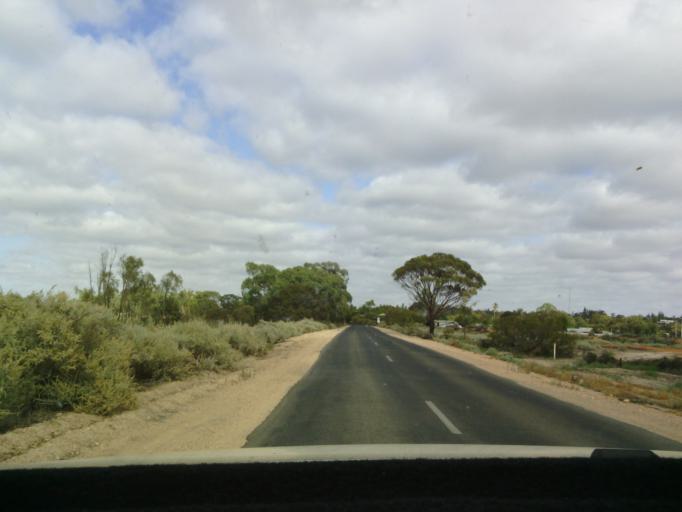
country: AU
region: South Australia
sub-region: Berri and Barmera
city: Berri
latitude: -34.2861
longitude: 140.6153
